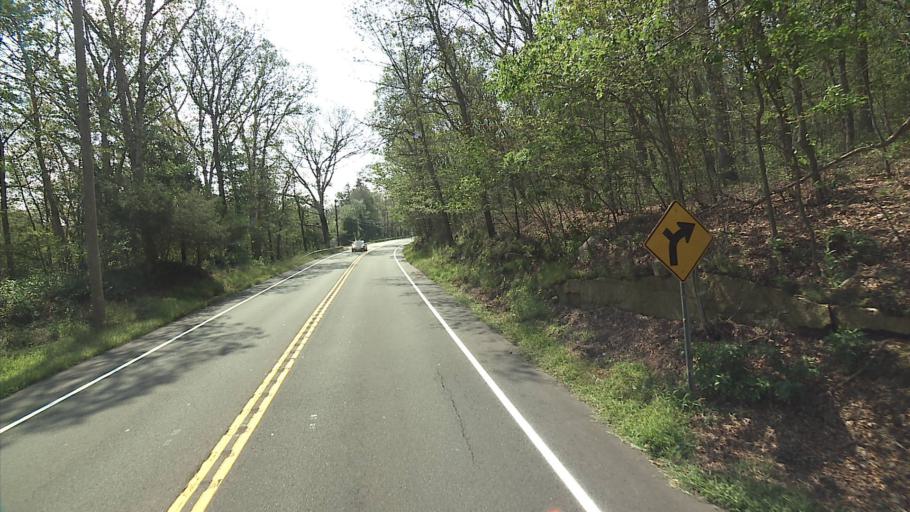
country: US
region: Connecticut
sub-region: Middlesex County
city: Durham
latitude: 41.4298
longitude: -72.6496
